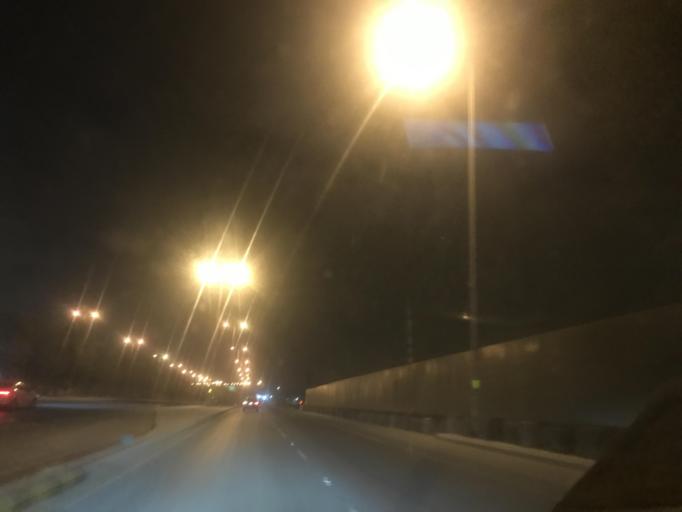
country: SA
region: Ar Riyad
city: Riyadh
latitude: 24.7897
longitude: 46.5889
